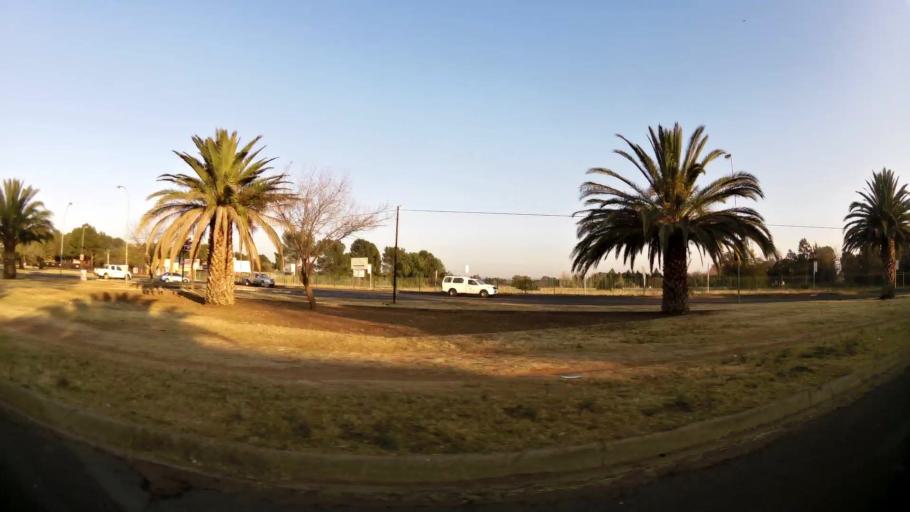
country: ZA
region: Orange Free State
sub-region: Mangaung Metropolitan Municipality
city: Bloemfontein
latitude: -29.0868
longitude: 26.1550
